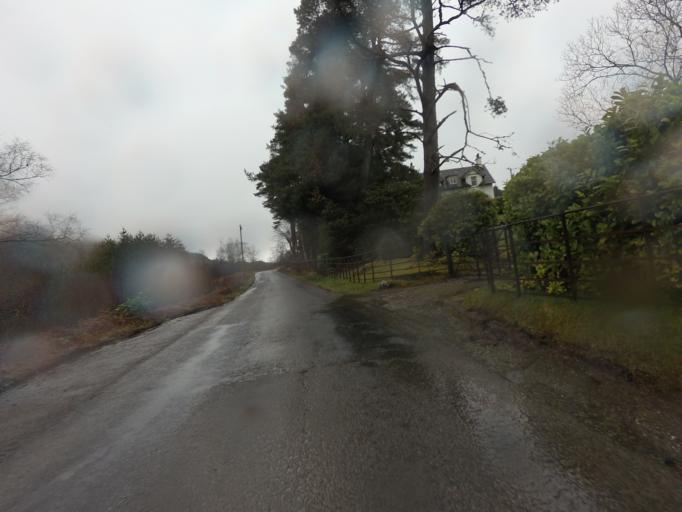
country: GB
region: Scotland
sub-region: West Dunbartonshire
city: Balloch
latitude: 56.2363
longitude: -4.5621
